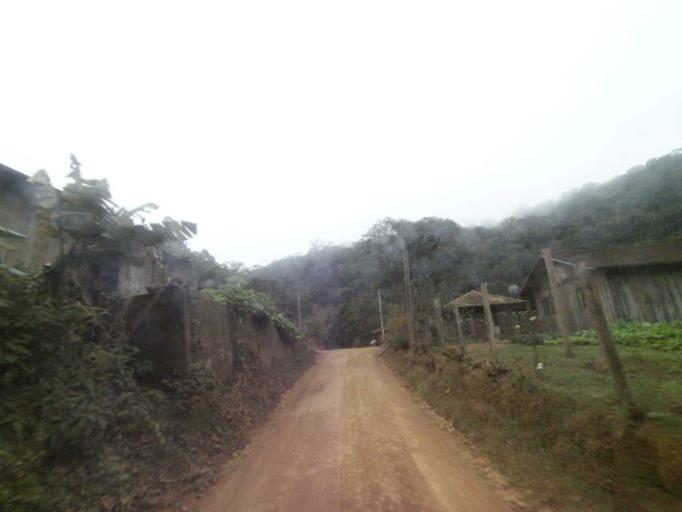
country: BR
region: Santa Catarina
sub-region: Anitapolis
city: Anitapolis
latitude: -27.8948
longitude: -49.1294
